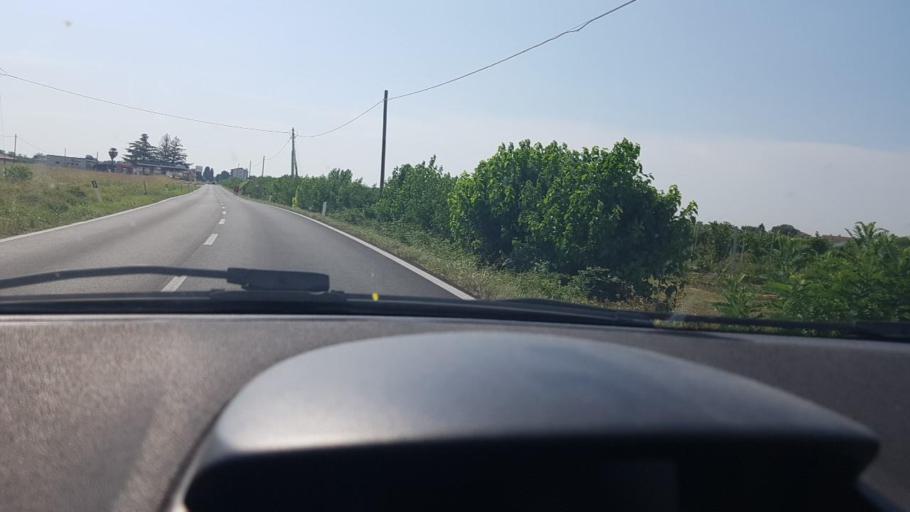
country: IT
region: Friuli Venezia Giulia
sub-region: Provincia di Udine
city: San Vito al Torre
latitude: 45.8922
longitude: 13.3785
